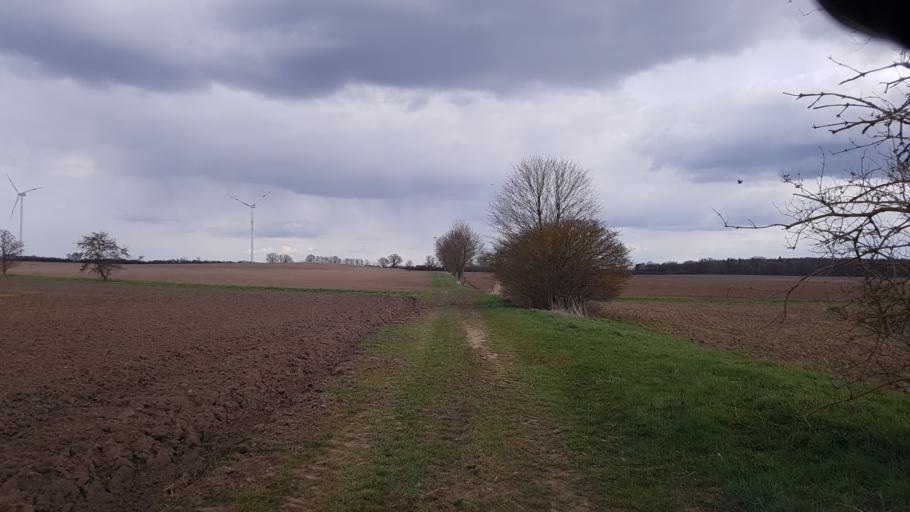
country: DE
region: Brandenburg
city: Hohenbucko
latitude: 51.6942
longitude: 13.4814
